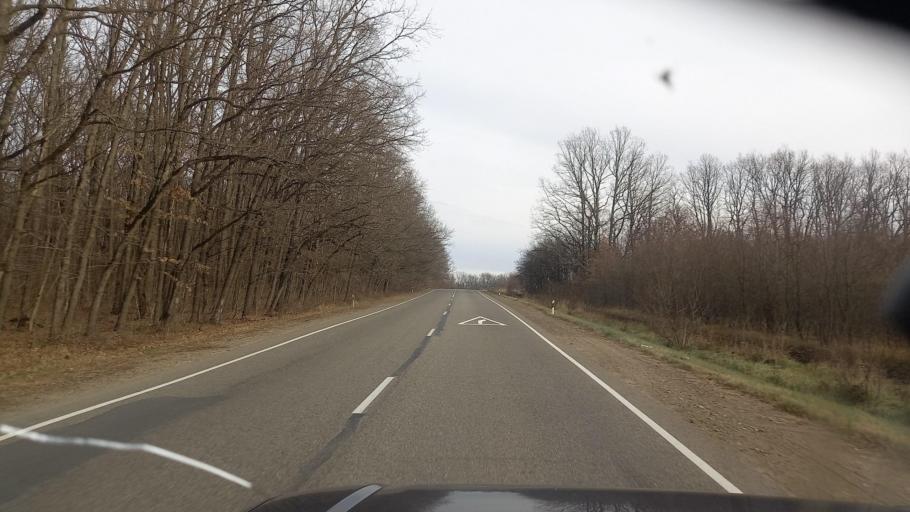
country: RU
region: Adygeya
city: Ponezhukay
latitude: 44.6739
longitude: 39.4487
